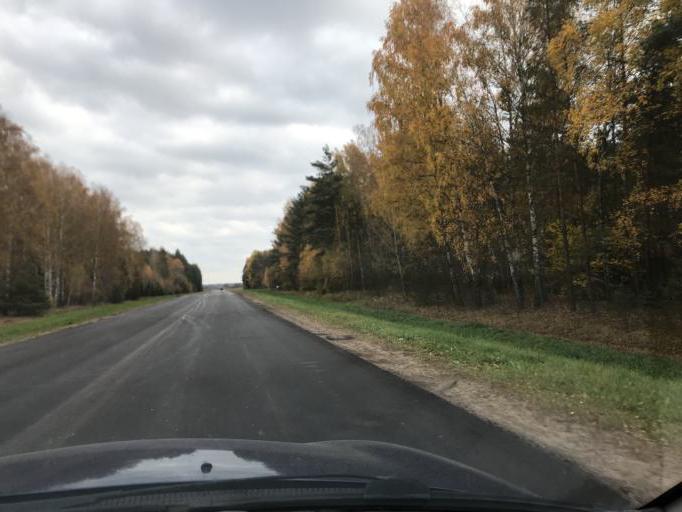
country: BY
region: Grodnenskaya
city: Lida
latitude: 53.7502
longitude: 25.2314
